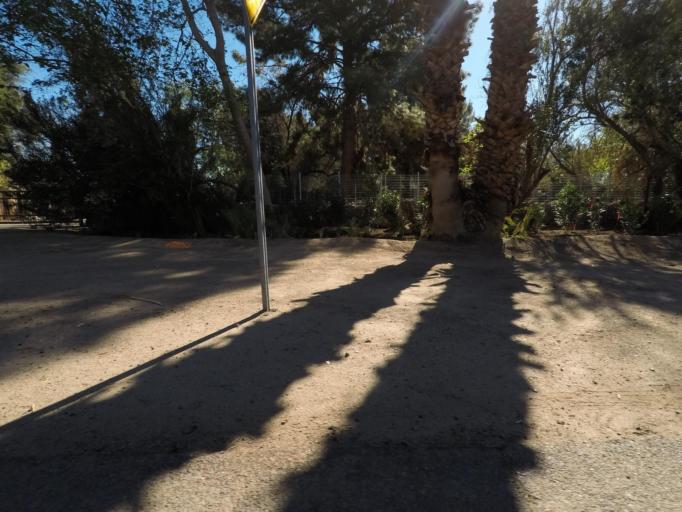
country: US
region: Arizona
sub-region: Maricopa County
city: Glendale
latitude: 33.5449
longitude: -112.1257
